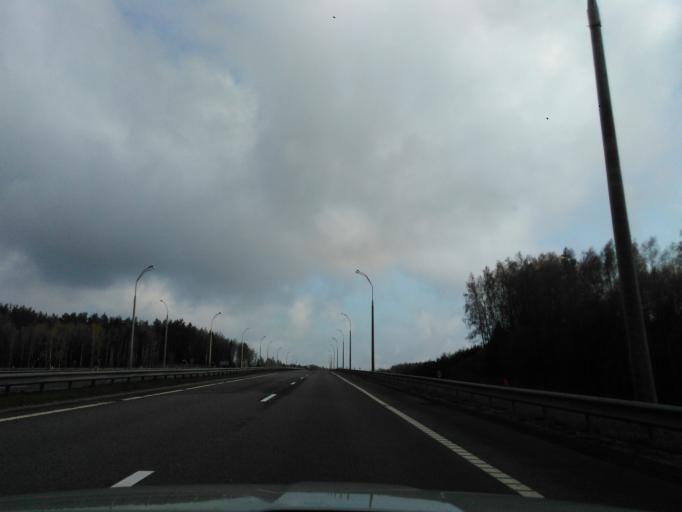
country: BY
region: Minsk
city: Lahoysk
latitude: 54.1807
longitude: 27.8180
